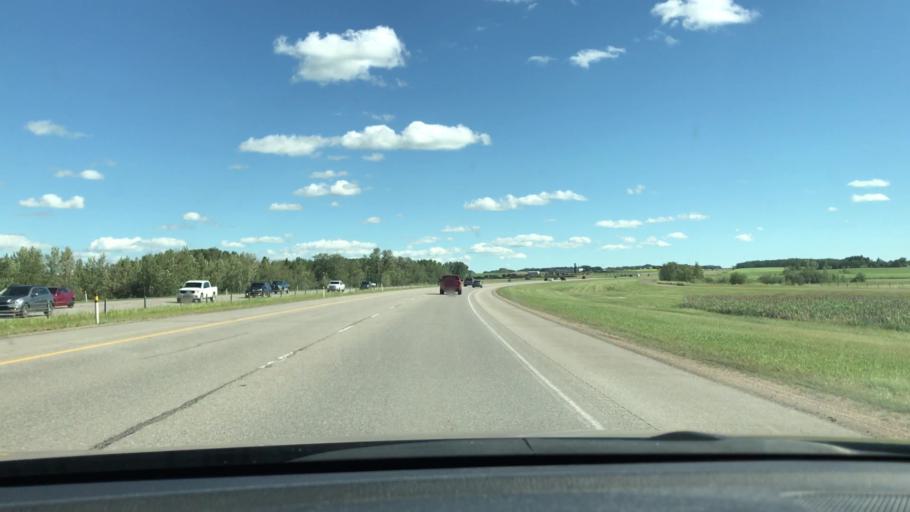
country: CA
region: Alberta
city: Penhold
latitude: 52.1825
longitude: -113.8158
